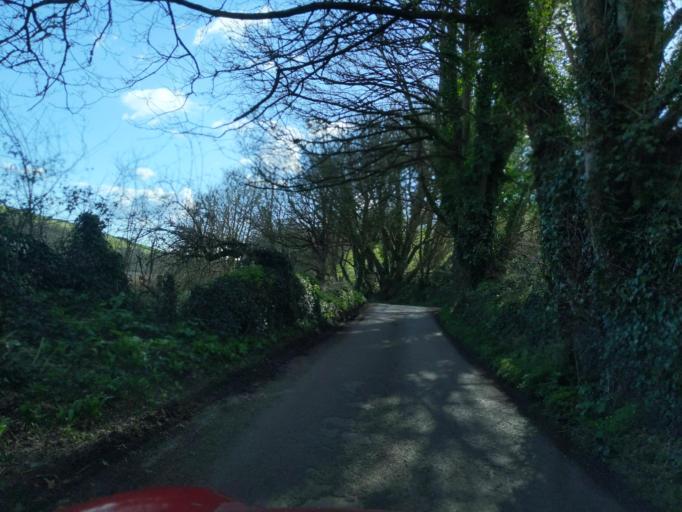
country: GB
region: England
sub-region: Devon
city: Kingsbridge
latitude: 50.2833
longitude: -3.7595
